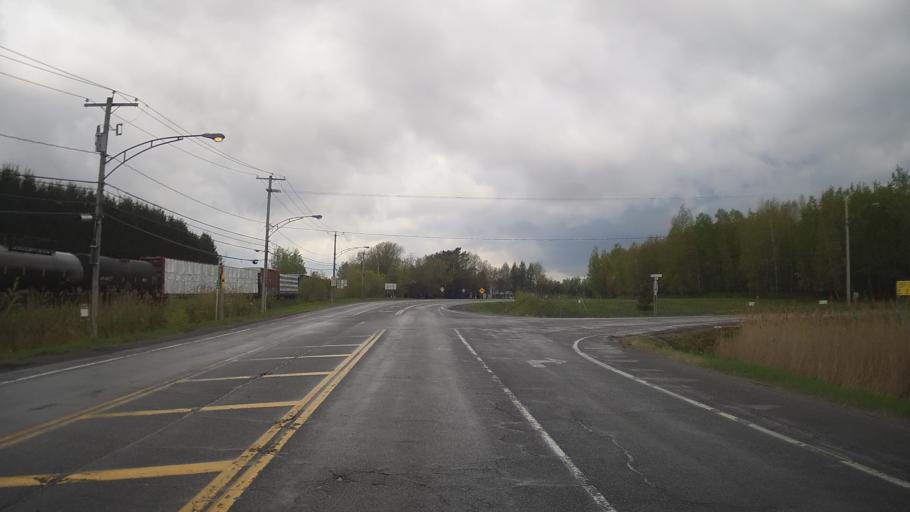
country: CA
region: Quebec
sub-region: Monteregie
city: Farnham
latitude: 45.2892
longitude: -73.0134
